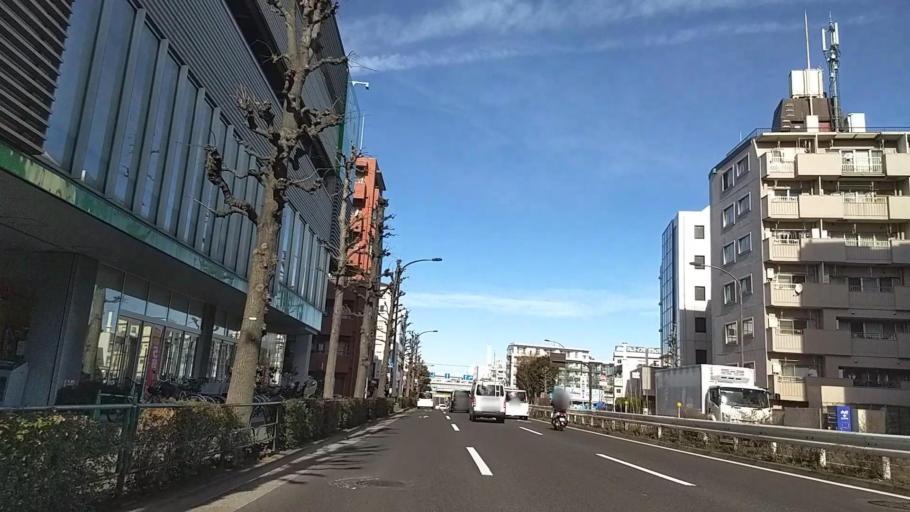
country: JP
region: Tokyo
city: Mitaka-shi
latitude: 35.6437
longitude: 139.6185
